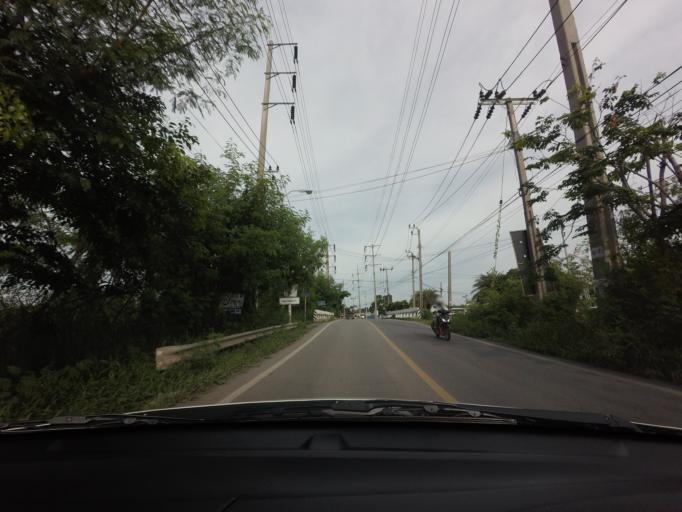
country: TH
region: Bangkok
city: Bang Na
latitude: 13.6179
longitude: 100.6635
